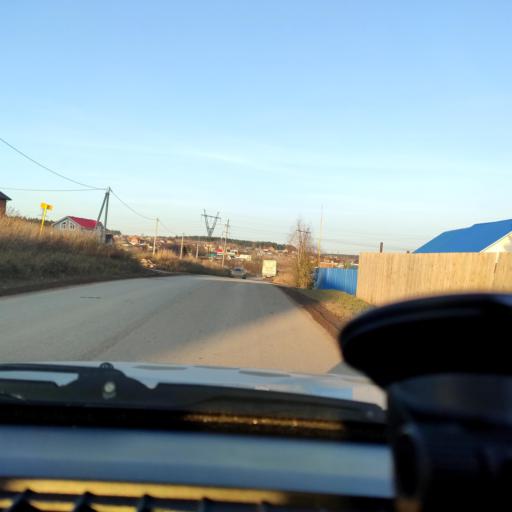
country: RU
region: Perm
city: Ferma
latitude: 57.9487
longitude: 56.3620
